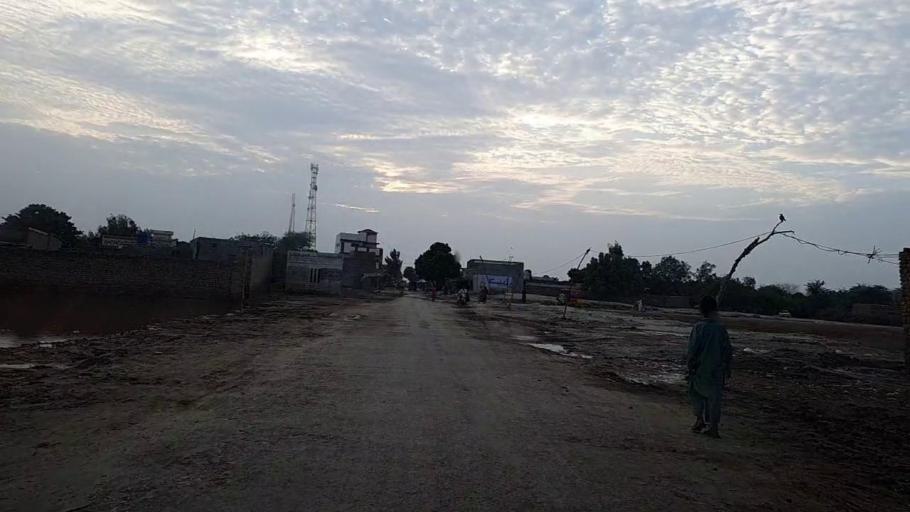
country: PK
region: Sindh
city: Naushahro Firoz
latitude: 26.8096
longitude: 68.2000
